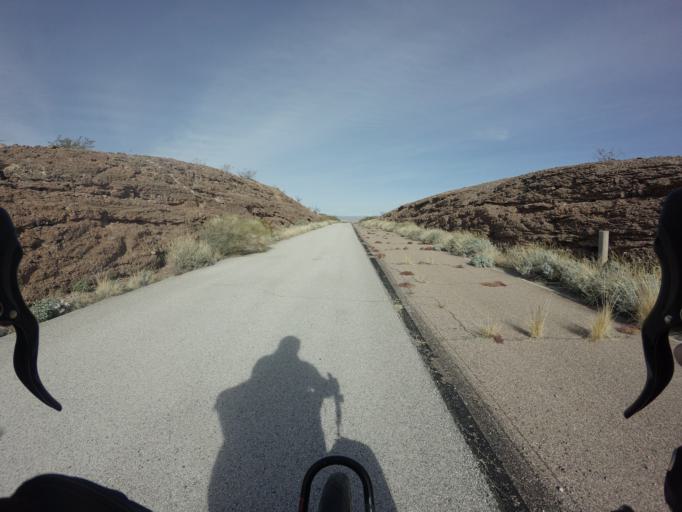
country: US
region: Nevada
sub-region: Clark County
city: Boulder City
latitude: 36.0920
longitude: -114.8411
